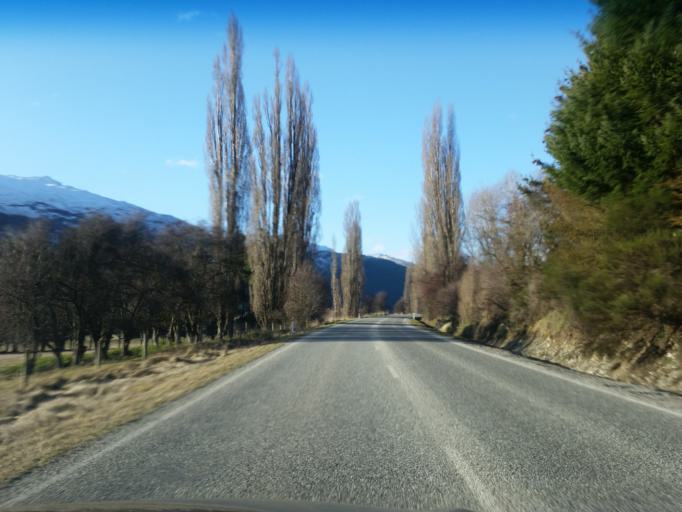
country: NZ
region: Otago
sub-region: Queenstown-Lakes District
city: Arrowtown
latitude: -44.9600
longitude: 168.7253
